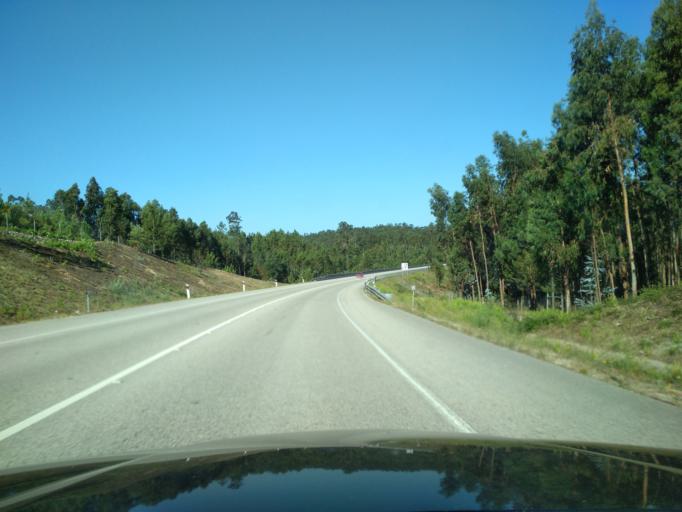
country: PT
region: Leiria
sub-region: Pombal
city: Lourical
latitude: 39.9855
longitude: -8.7620
